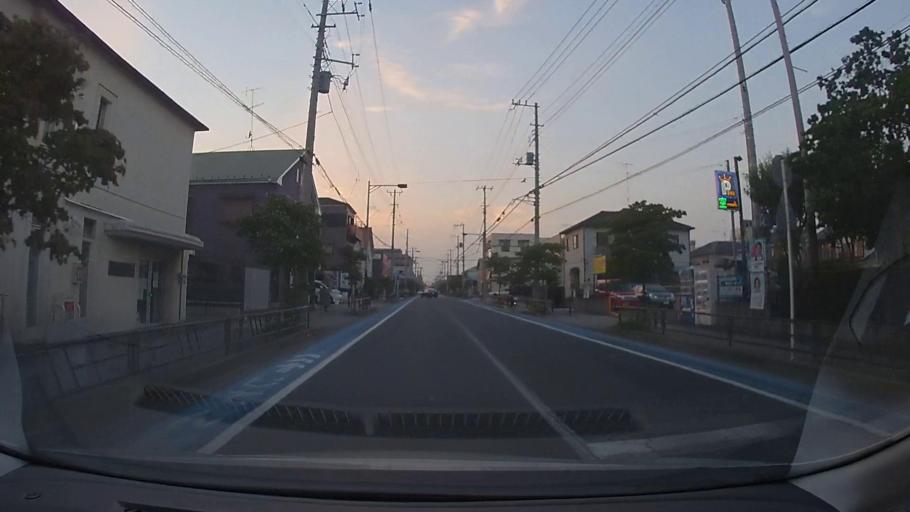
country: JP
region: Kanagawa
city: Minami-rinkan
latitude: 35.4894
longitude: 139.4481
